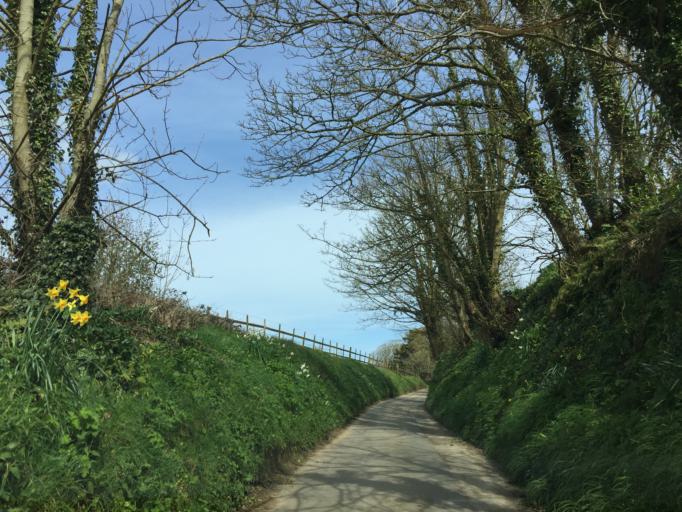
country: JE
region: St Helier
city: Saint Helier
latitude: 49.2367
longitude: -2.1857
